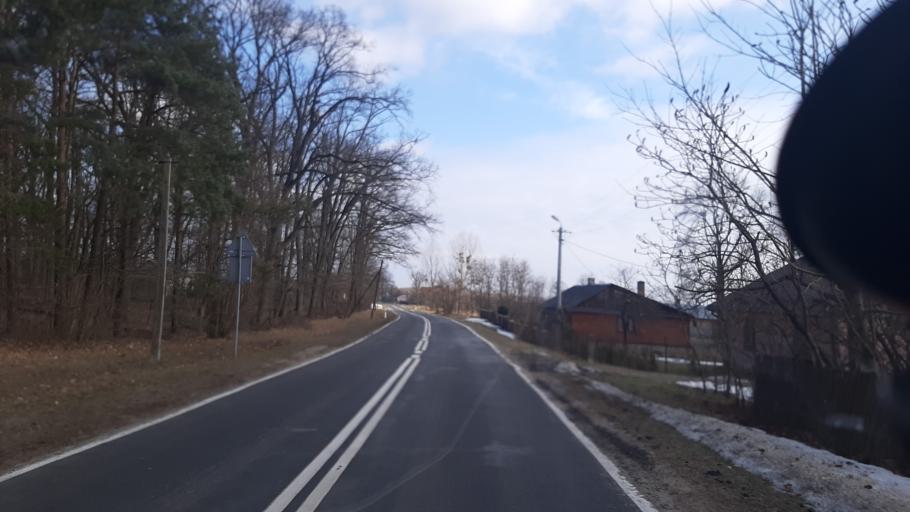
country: PL
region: Lublin Voivodeship
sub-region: Powiat wlodawski
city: Urszulin
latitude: 51.4943
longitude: 23.2211
